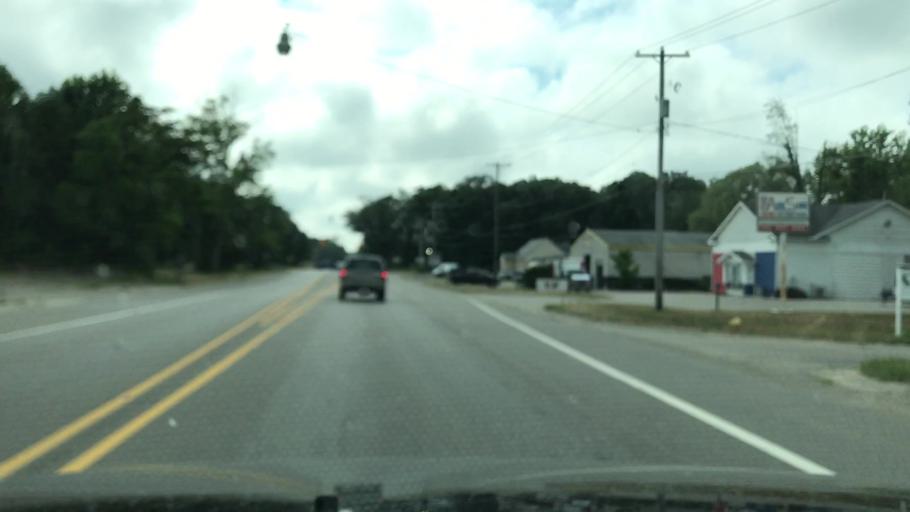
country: US
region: Michigan
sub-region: Ottawa County
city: Spring Lake
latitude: 43.0740
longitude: -86.1536
